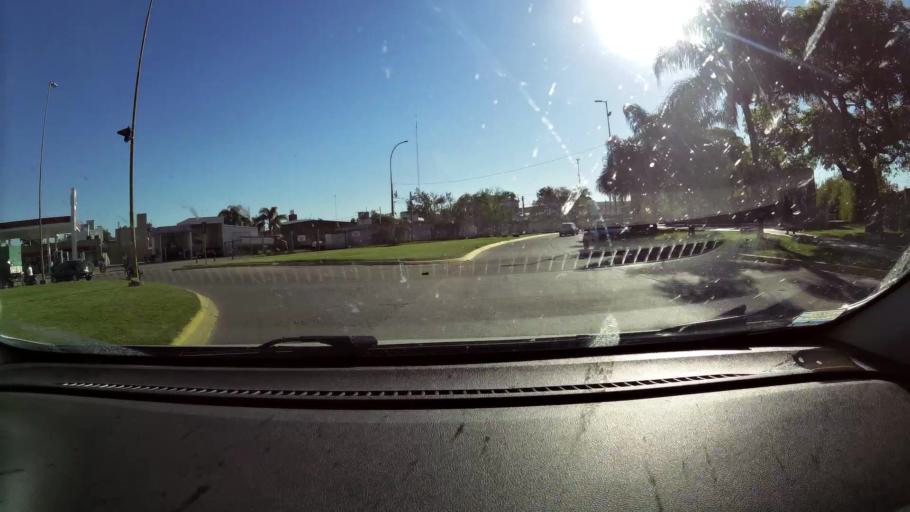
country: AR
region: Cordoba
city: San Francisco
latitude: -31.4283
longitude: -62.0974
